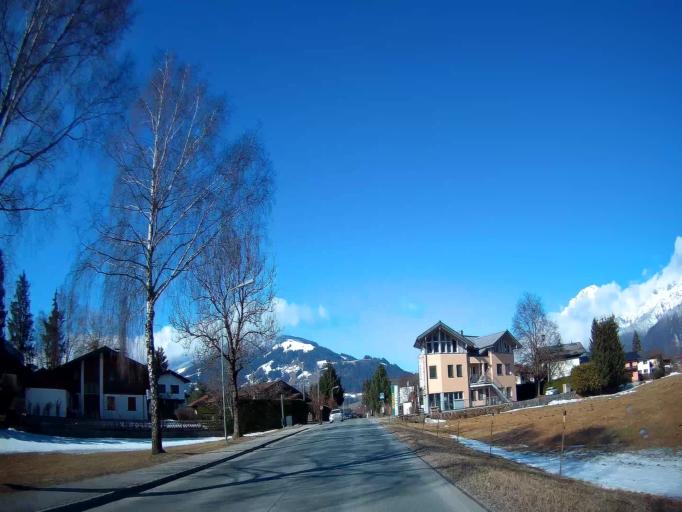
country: AT
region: Salzburg
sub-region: Politischer Bezirk Zell am See
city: Saalfelden am Steinernen Meer
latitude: 47.4332
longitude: 12.8478
